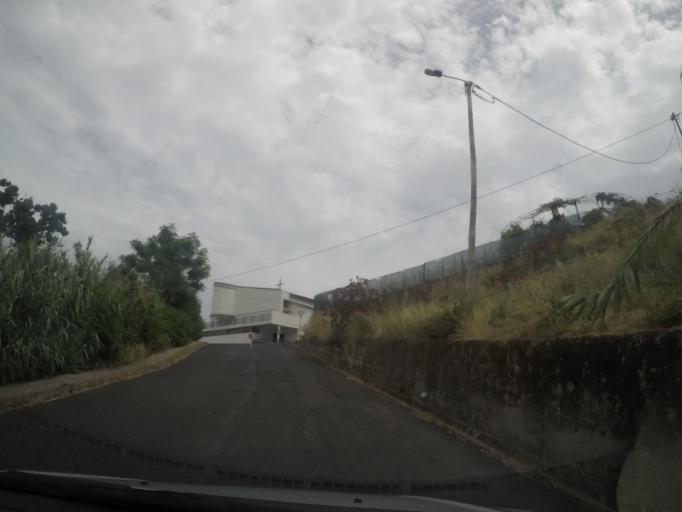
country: PT
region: Madeira
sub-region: Santa Cruz
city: Santa Cruz
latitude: 32.6753
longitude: -16.8117
